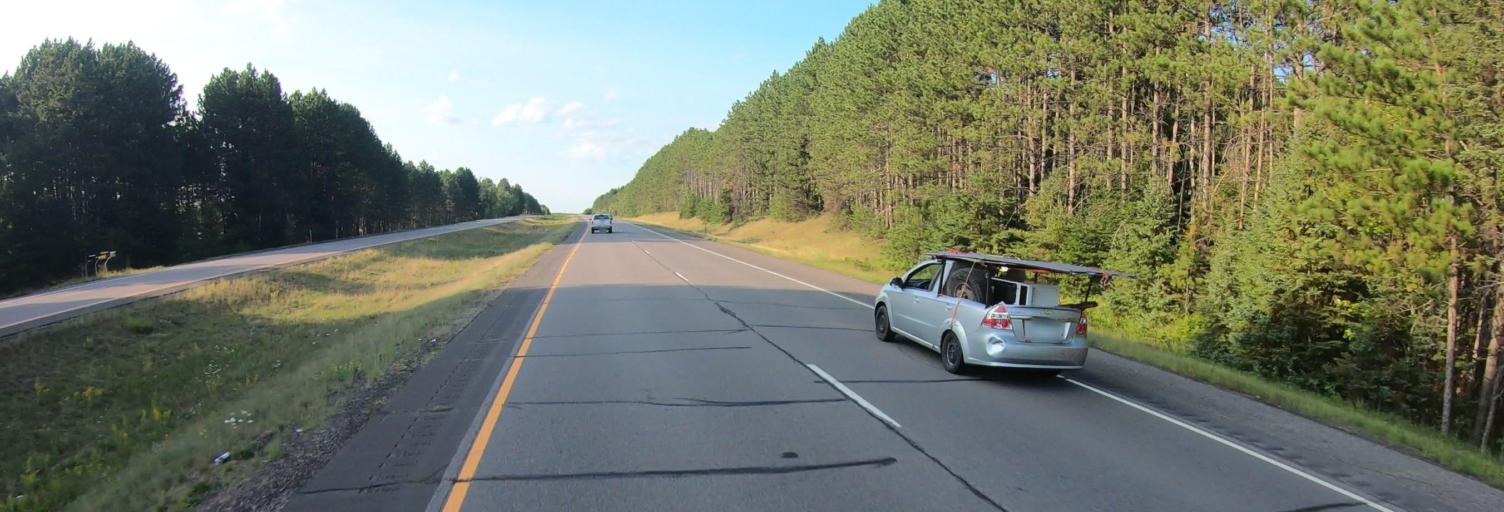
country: US
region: Minnesota
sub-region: Saint Louis County
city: Eveleth
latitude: 47.4114
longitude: -92.5211
